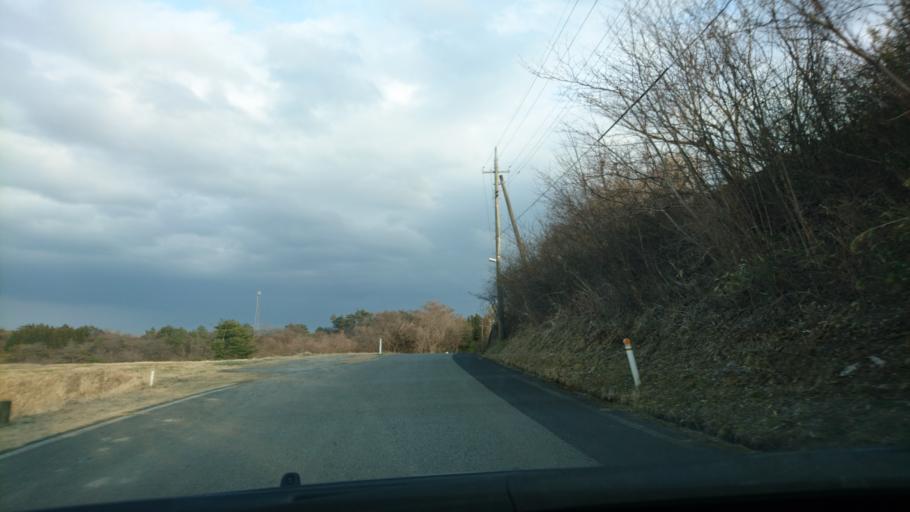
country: JP
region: Iwate
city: Ichinoseki
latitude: 38.8942
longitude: 141.2381
